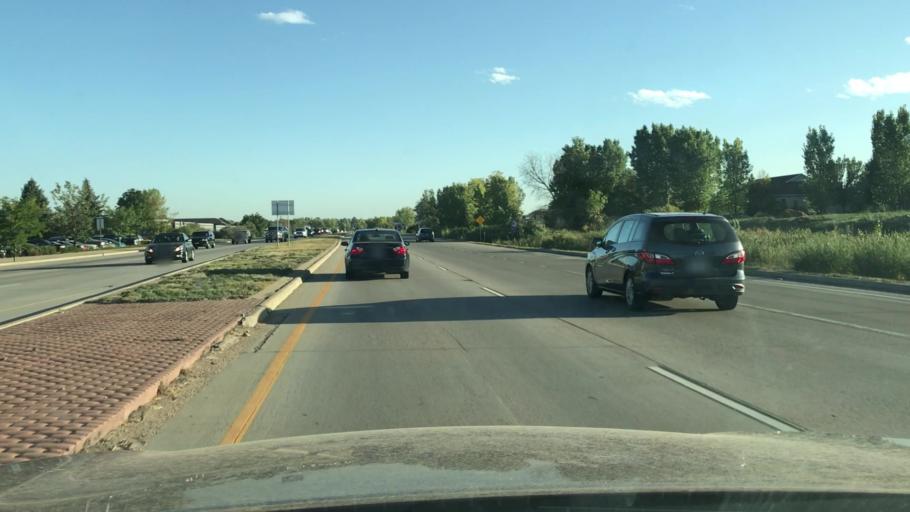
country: US
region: Colorado
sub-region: Boulder County
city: Lafayette
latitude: 39.9859
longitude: -105.0985
